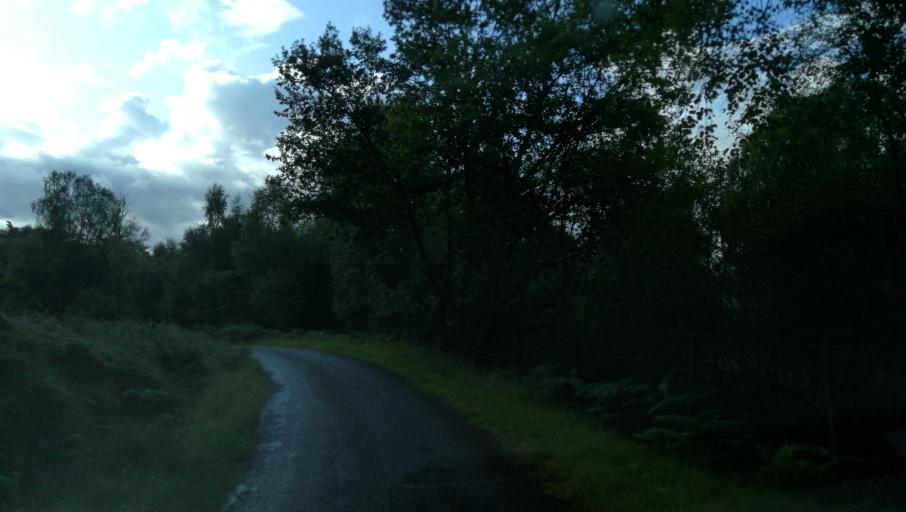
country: GB
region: Scotland
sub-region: Highland
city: Spean Bridge
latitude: 57.0694
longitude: -4.8248
